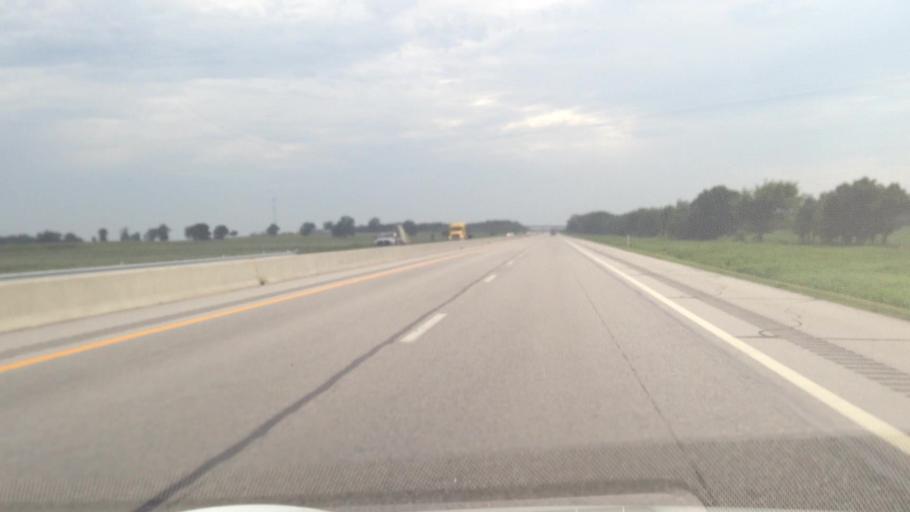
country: US
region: Kansas
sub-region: Cherokee County
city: Baxter Springs
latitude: 36.9550
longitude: -94.6703
